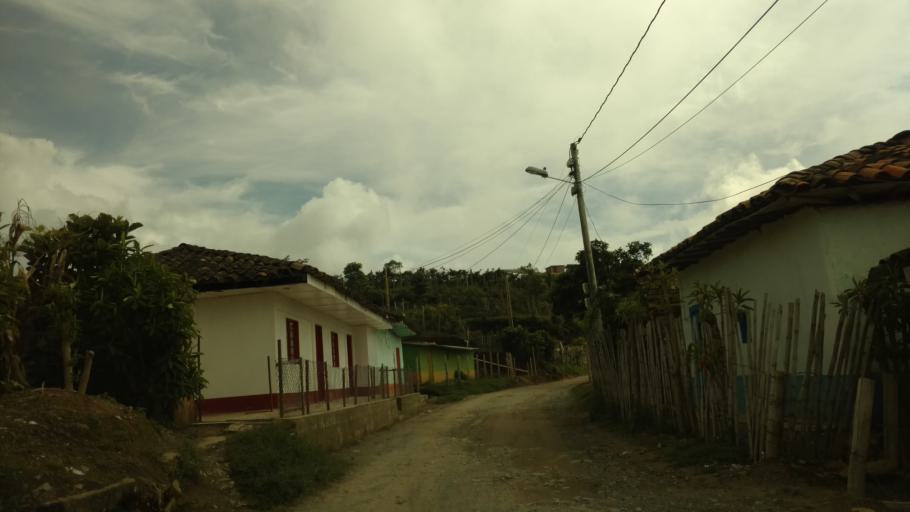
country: CO
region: Caldas
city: Aguadas
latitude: 5.6253
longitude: -75.4525
